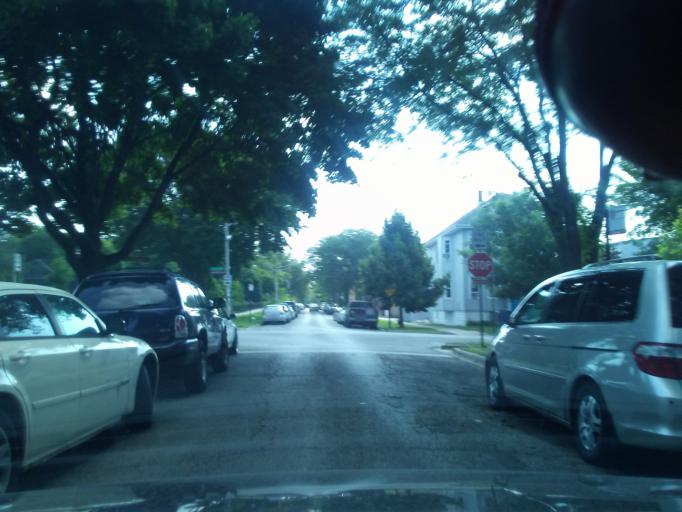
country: US
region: Illinois
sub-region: Cook County
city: Oak Park
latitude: 41.9223
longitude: -87.7540
